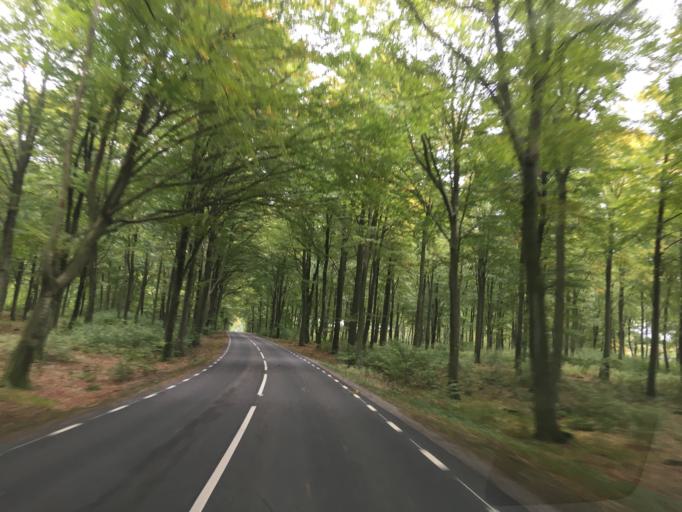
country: SE
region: Skane
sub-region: Simrishamns Kommun
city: Kivik
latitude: 55.6333
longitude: 14.0939
